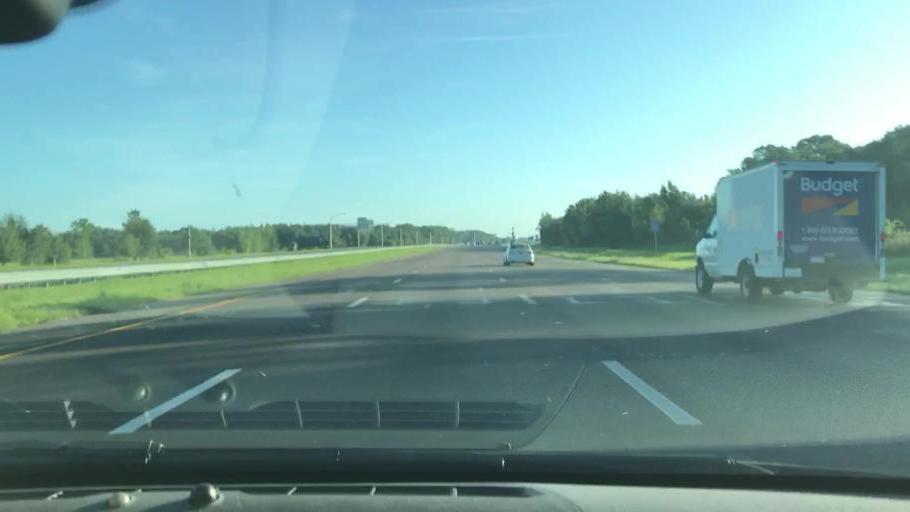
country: US
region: Florida
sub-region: Pasco County
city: Wesley Chapel
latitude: 28.2043
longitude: -82.3781
